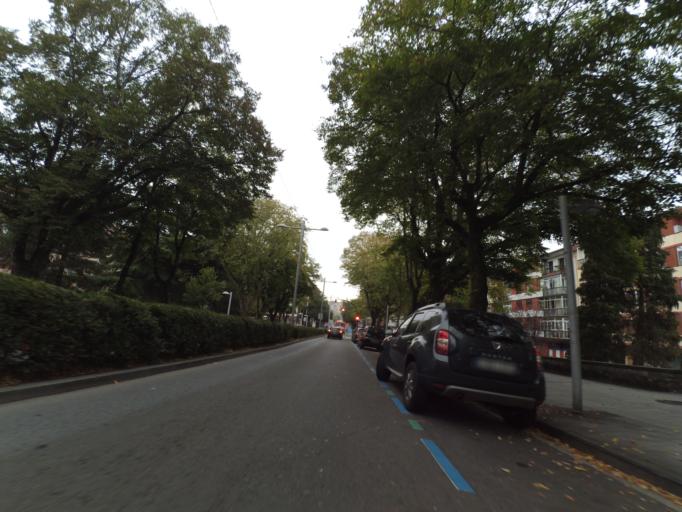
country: ES
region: Basque Country
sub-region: Provincia de Guipuzcoa
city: Irun
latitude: 43.3393
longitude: -1.7857
